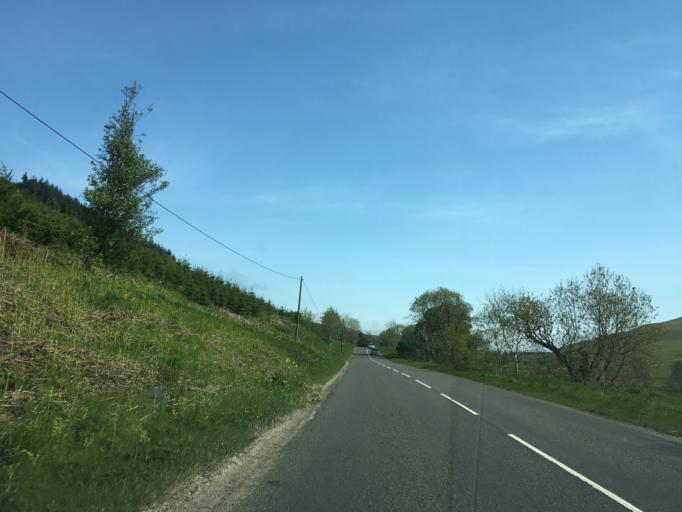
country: GB
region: Scotland
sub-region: South Lanarkshire
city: Biggar
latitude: 55.6591
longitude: -3.4308
